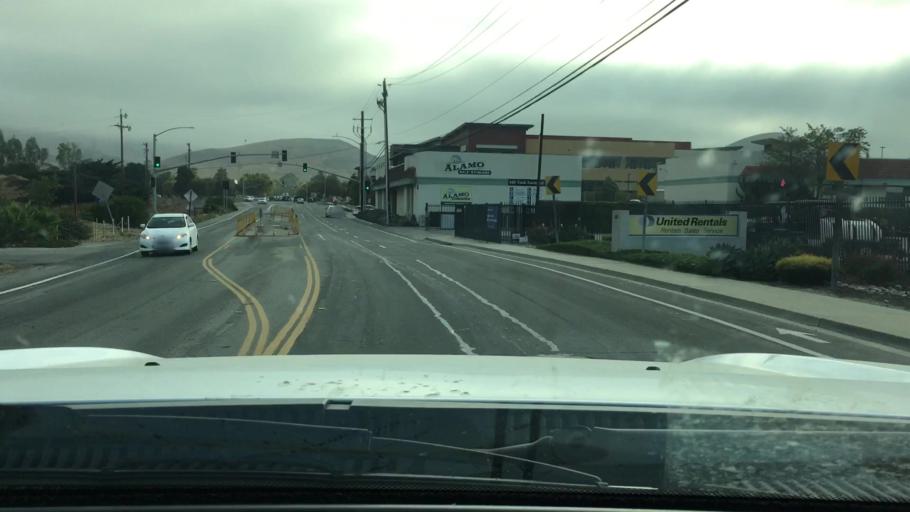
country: US
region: California
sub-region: San Luis Obispo County
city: San Luis Obispo
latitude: 35.2467
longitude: -120.6480
